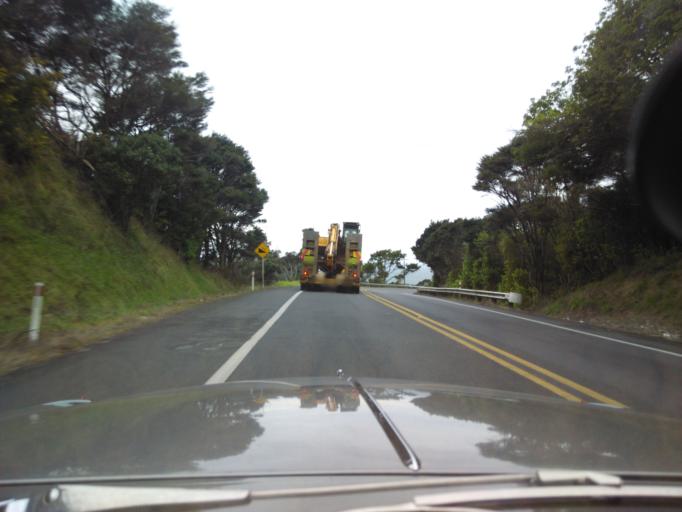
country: NZ
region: Auckland
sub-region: Auckland
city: Warkworth
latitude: -36.5336
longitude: 174.6892
